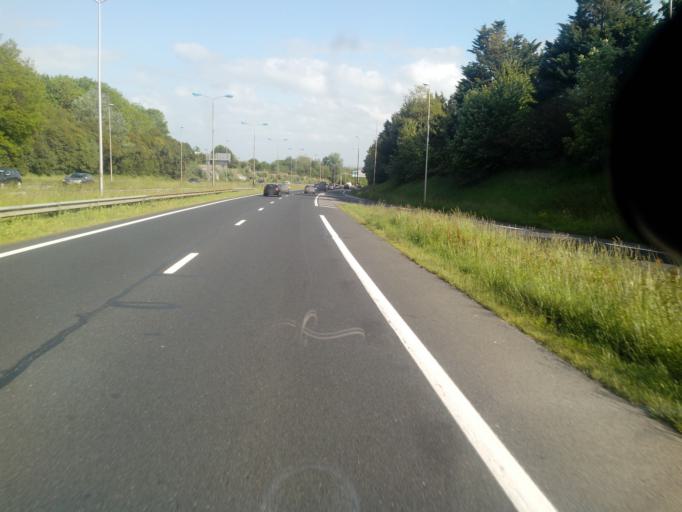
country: FR
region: Lower Normandy
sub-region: Departement du Calvados
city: Caen
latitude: 49.1984
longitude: -0.3427
